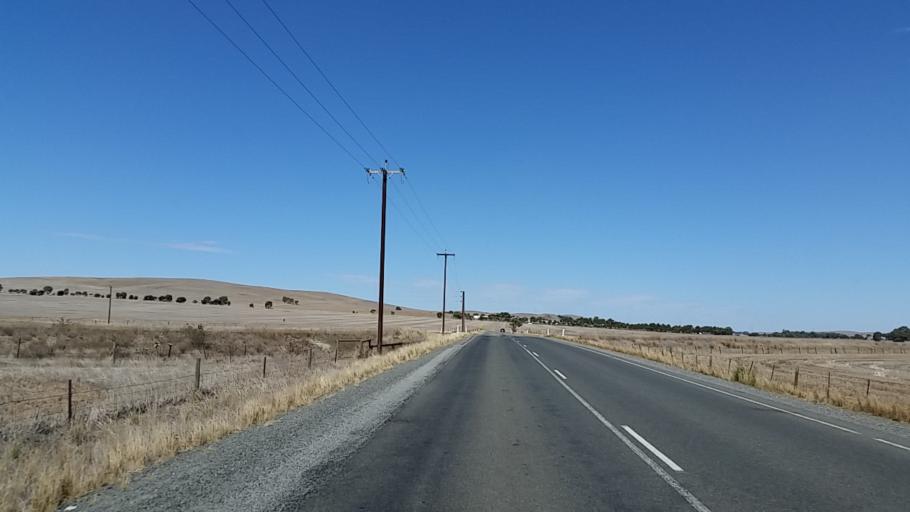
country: AU
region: South Australia
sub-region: Clare and Gilbert Valleys
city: Clare
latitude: -33.6876
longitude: 138.9067
